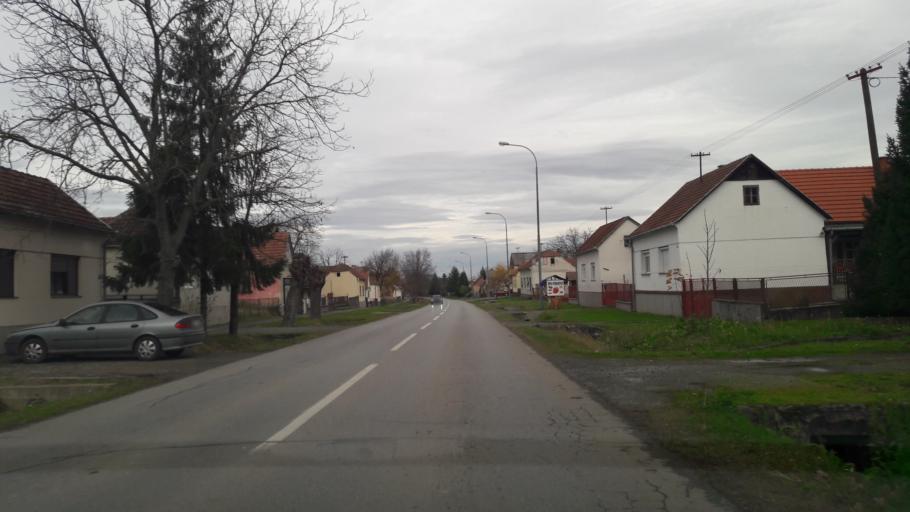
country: HR
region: Virovitick-Podravska
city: Orahovica
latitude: 45.5419
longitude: 17.8974
